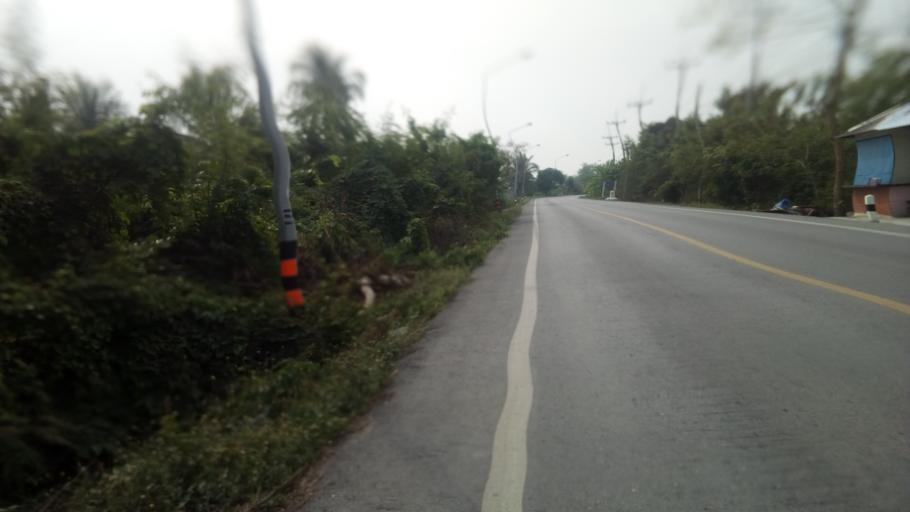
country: TH
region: Pathum Thani
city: Ban Rangsit
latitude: 14.0359
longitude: 100.8243
